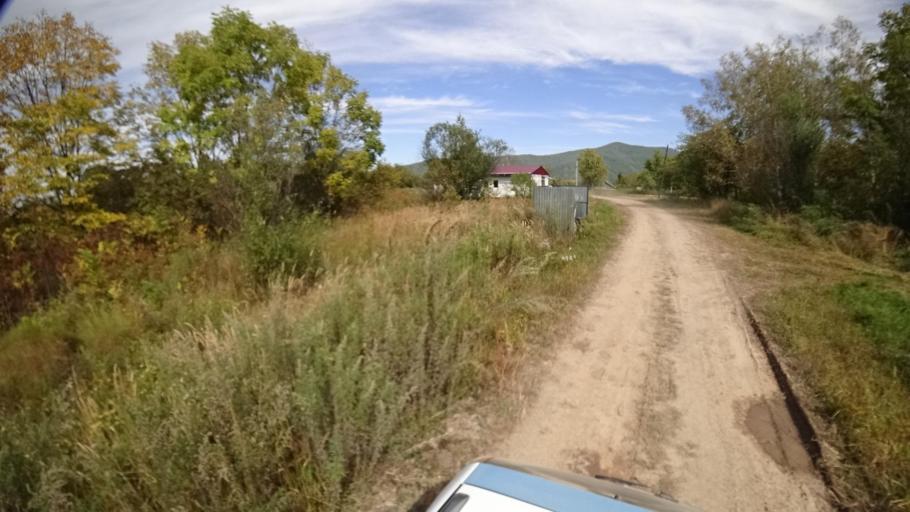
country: RU
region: Primorskiy
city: Yakovlevka
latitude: 44.6548
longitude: 133.7437
